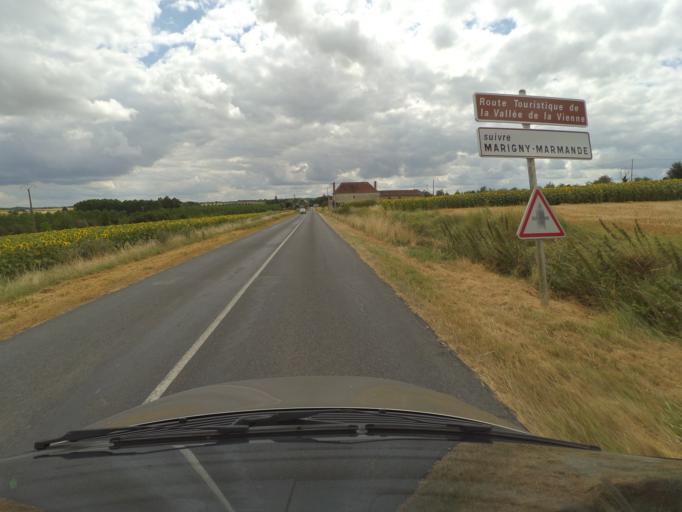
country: FR
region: Poitou-Charentes
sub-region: Departement de la Vienne
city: Saint-Gervais-les-Trois-Clochers
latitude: 46.9541
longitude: 0.4029
